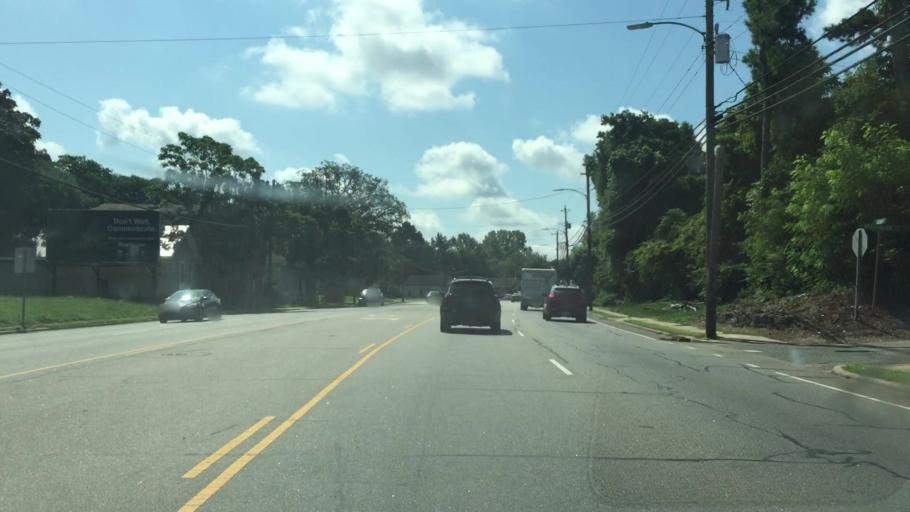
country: US
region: North Carolina
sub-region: Anson County
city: Wadesboro
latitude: 34.9713
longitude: -80.0803
